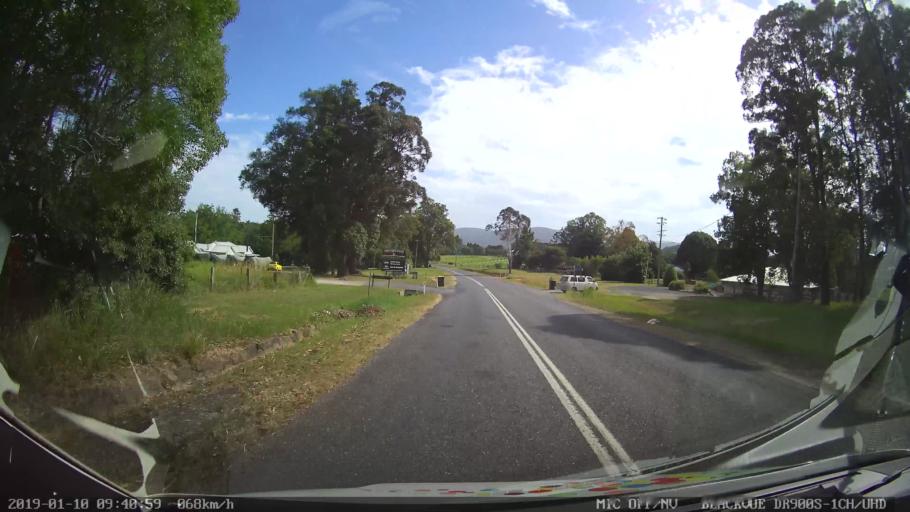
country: AU
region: New South Wales
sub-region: Coffs Harbour
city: Nana Glen
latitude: -30.1460
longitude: 153.0067
